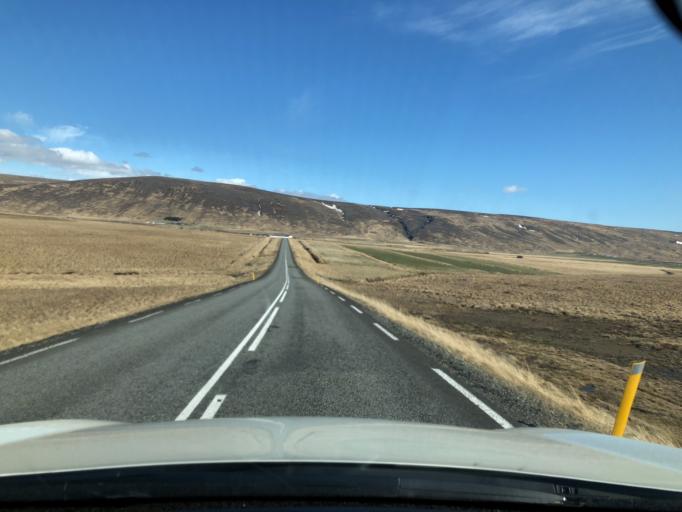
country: IS
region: South
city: Hveragerdi
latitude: 64.6846
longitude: -21.2405
